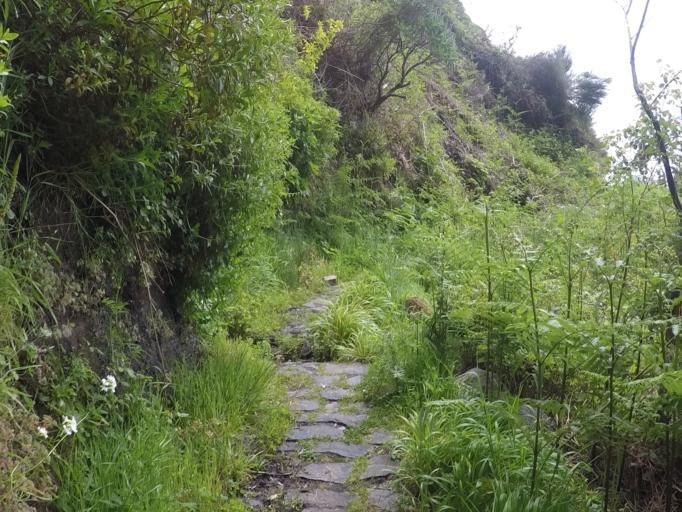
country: PT
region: Madeira
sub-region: Camara de Lobos
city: Curral das Freiras
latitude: 32.7368
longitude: -16.9998
